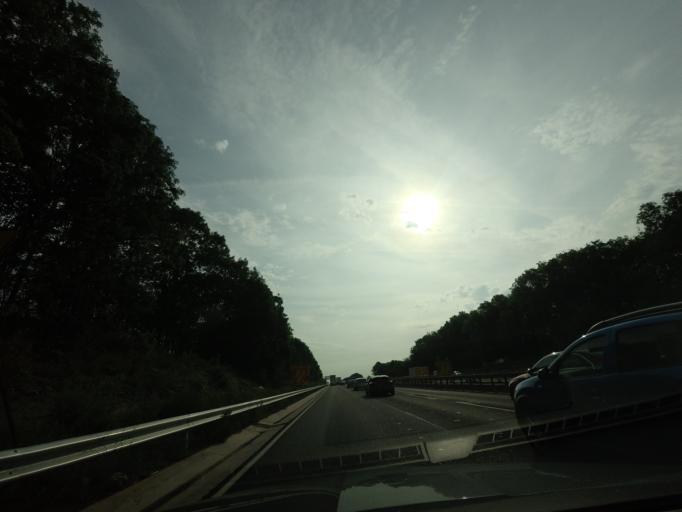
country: GB
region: England
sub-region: Coventry
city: Keresley
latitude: 52.4691
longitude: -1.5769
